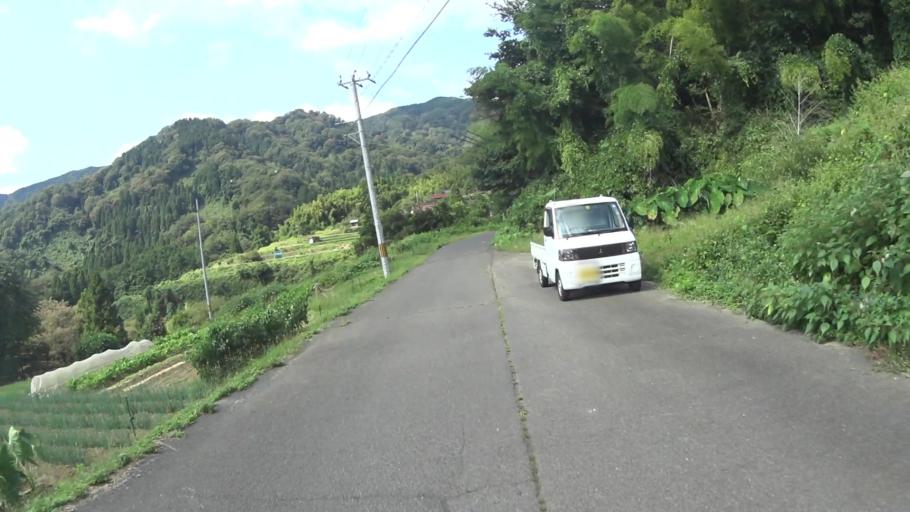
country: JP
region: Kyoto
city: Miyazu
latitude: 35.6809
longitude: 135.2364
